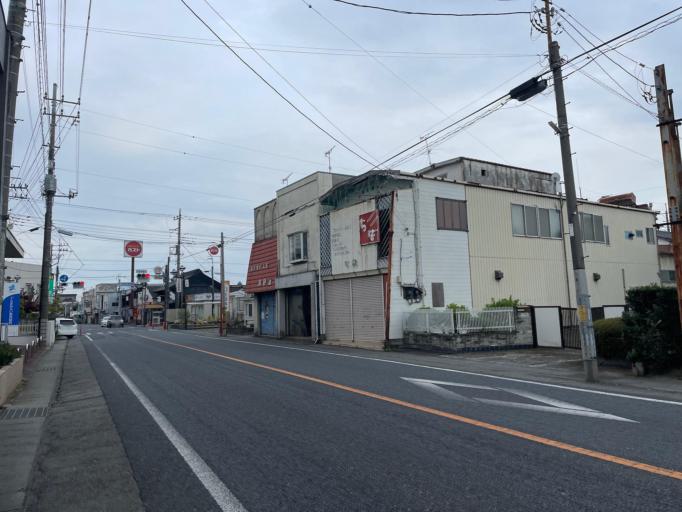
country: JP
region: Gunma
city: Sakai-nakajima
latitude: 36.2743
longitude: 139.2545
